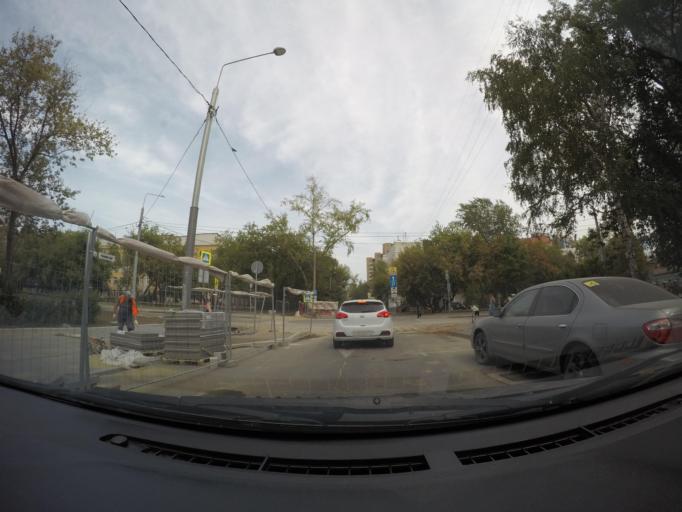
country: RU
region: Moscow
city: Sokol'niki
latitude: 55.7851
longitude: 37.6852
